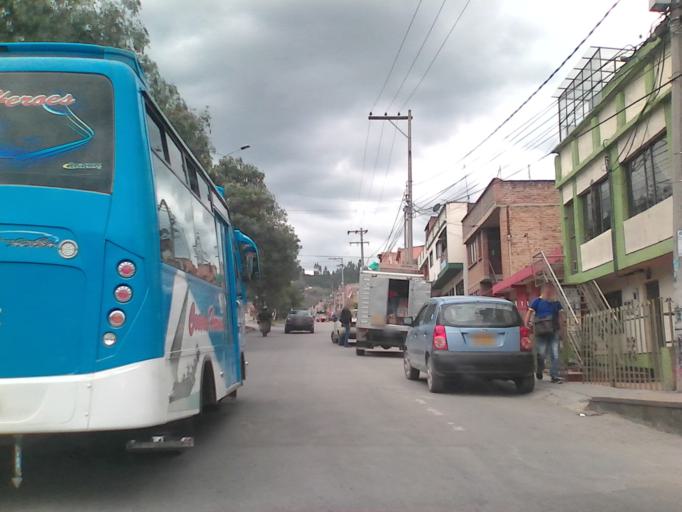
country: CO
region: Boyaca
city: Duitama
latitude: 5.8258
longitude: -73.0435
